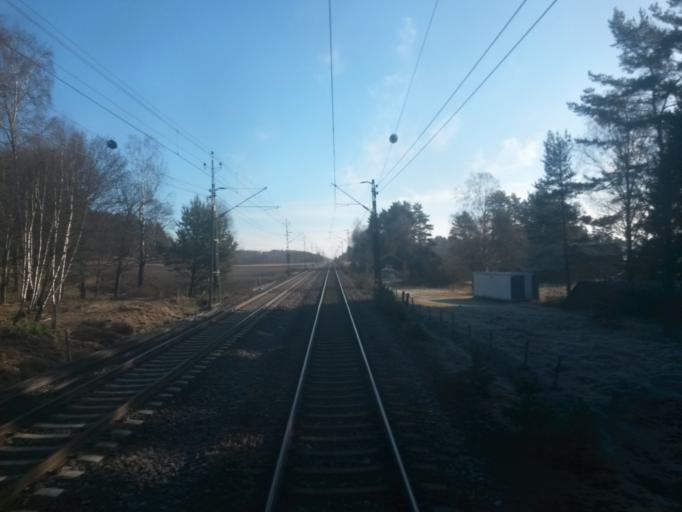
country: SE
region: Vaestra Goetaland
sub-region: Vargarda Kommun
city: Vargarda
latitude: 58.0348
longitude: 12.8415
